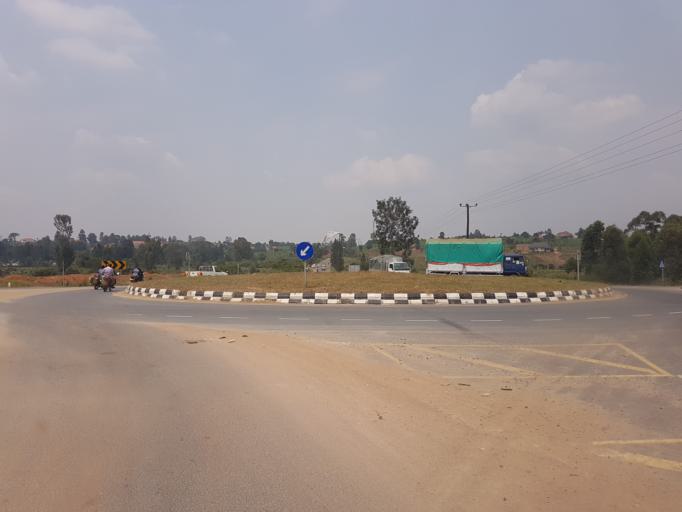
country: UG
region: Western Region
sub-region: Mbarara District
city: Bwizibwera
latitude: -0.6026
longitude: 30.6186
